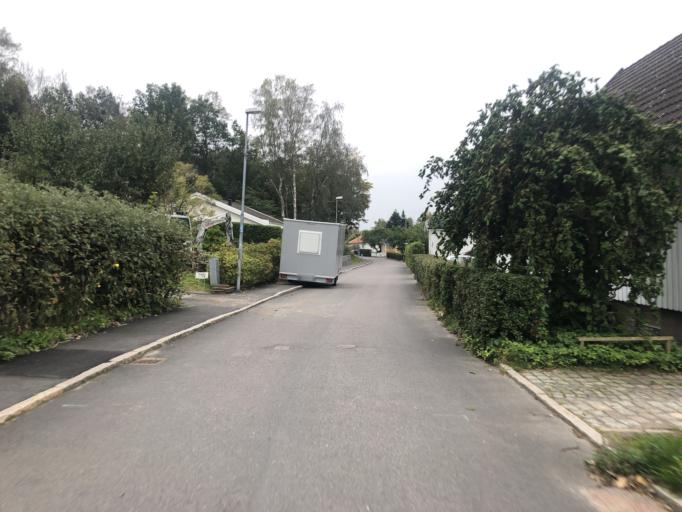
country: SE
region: Vaestra Goetaland
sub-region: Molndal
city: Moelndal
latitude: 57.6615
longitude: 12.0290
